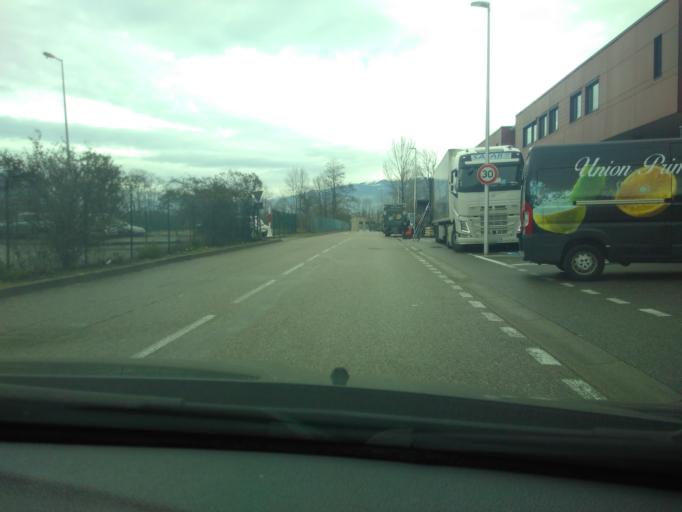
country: FR
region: Rhone-Alpes
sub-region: Departement de l'Isere
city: Montbonnot-Saint-Martin
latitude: 45.2192
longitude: 5.8146
